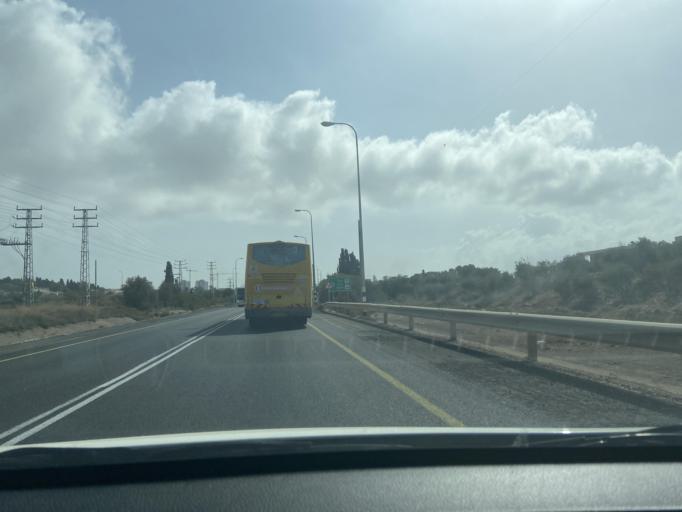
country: IL
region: Northern District
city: Nahariya
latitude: 33.0288
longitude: 35.1041
